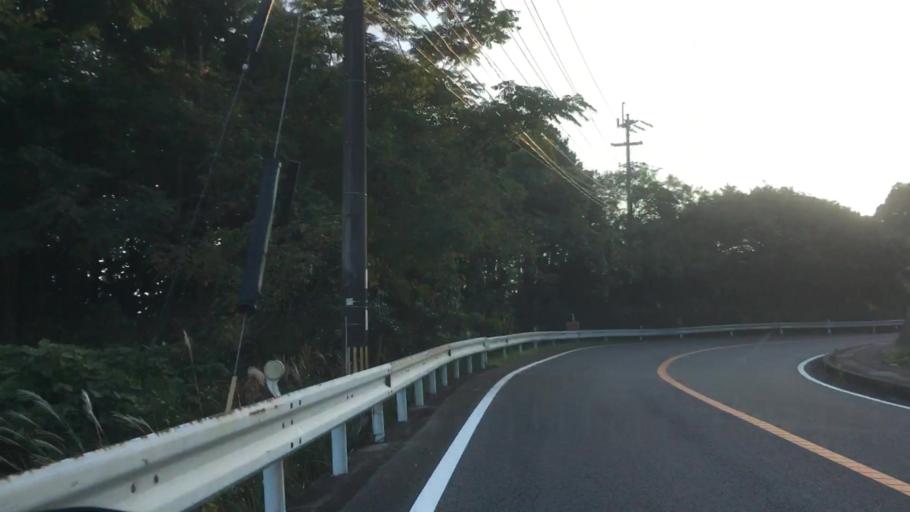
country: JP
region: Nagasaki
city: Sasebo
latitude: 32.9911
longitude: 129.7240
